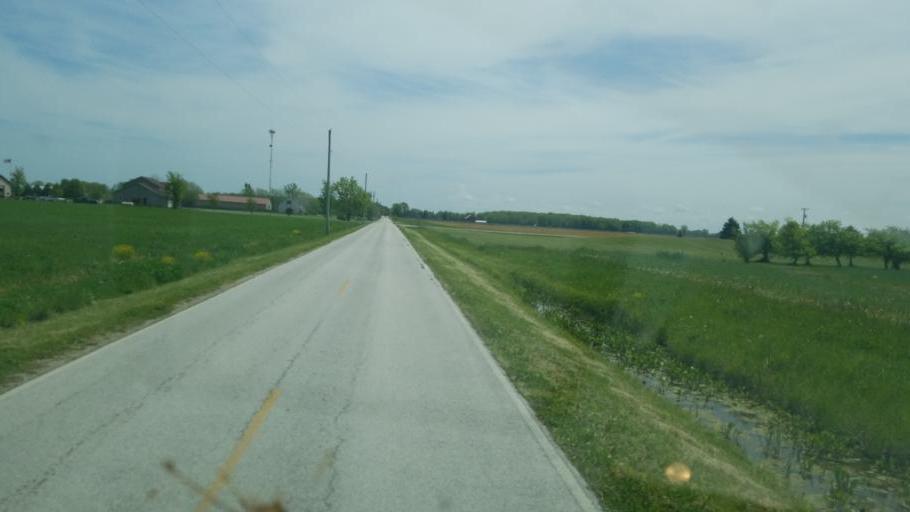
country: US
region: Ohio
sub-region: Ottawa County
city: Oak Harbor
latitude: 41.4869
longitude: -83.1568
